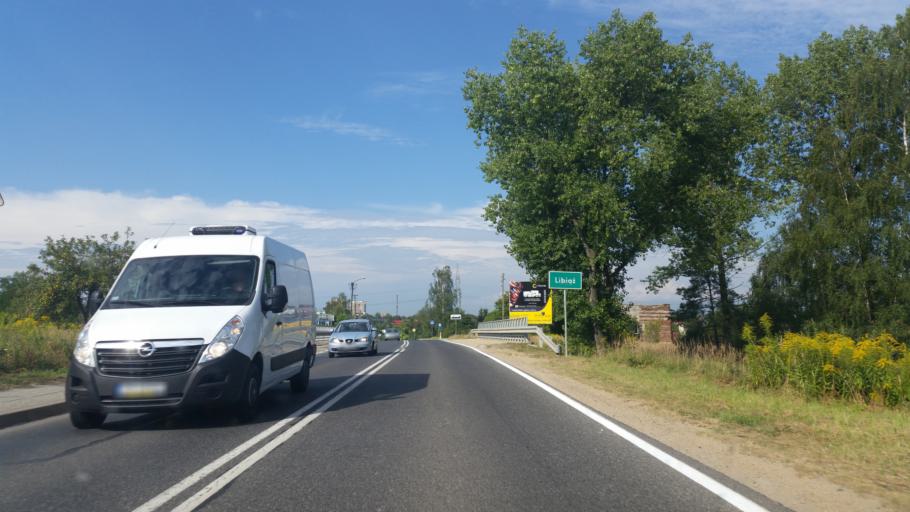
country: PL
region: Lesser Poland Voivodeship
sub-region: Powiat chrzanowski
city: Libiaz
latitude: 50.1104
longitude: 19.3400
